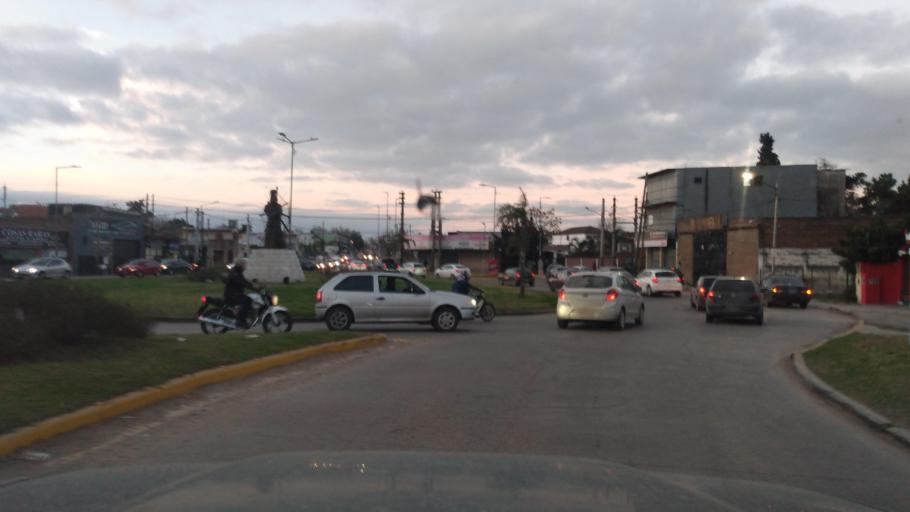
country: AR
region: Buenos Aires
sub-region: Partido de Pilar
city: Pilar
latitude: -34.4677
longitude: -58.9163
